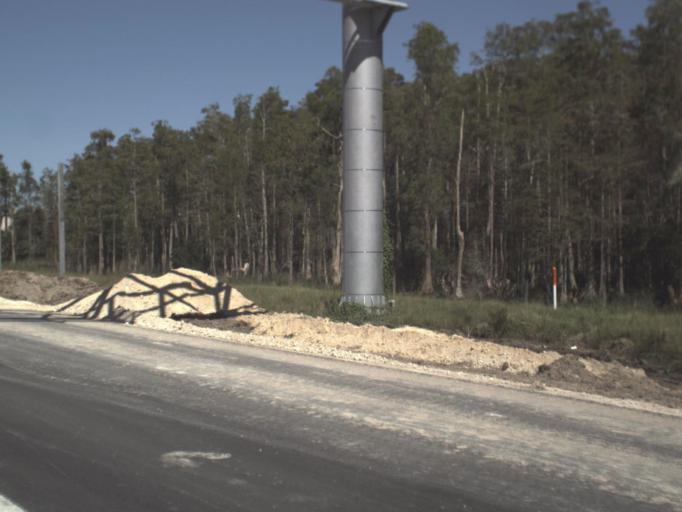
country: US
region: Florida
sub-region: Lee County
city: Three Oaks
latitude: 26.5316
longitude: -81.7947
